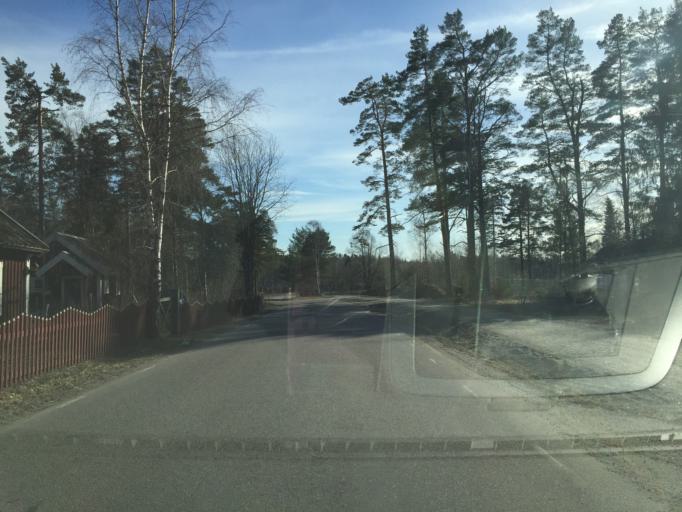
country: SE
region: Stockholm
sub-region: Nynashamns Kommun
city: Osmo
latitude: 59.0565
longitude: 17.8709
